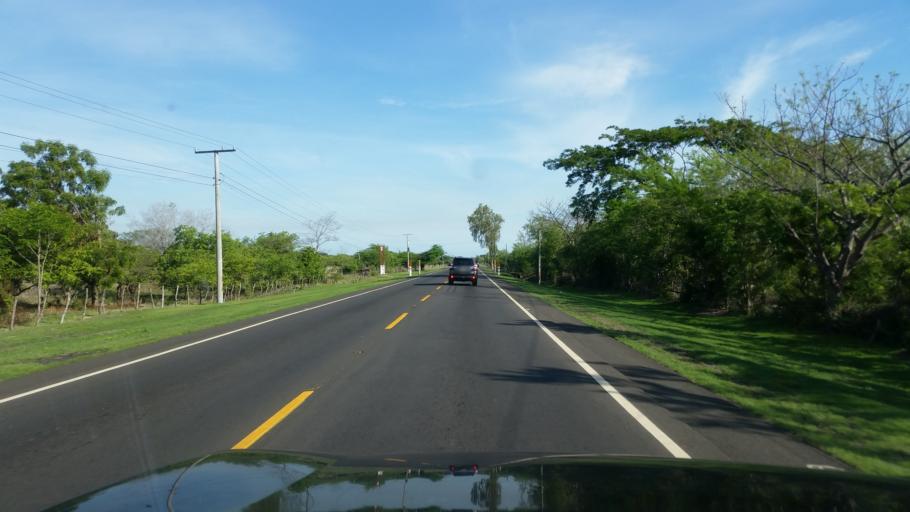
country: NI
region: Leon
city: La Paz Centro
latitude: 12.2838
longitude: -86.7540
